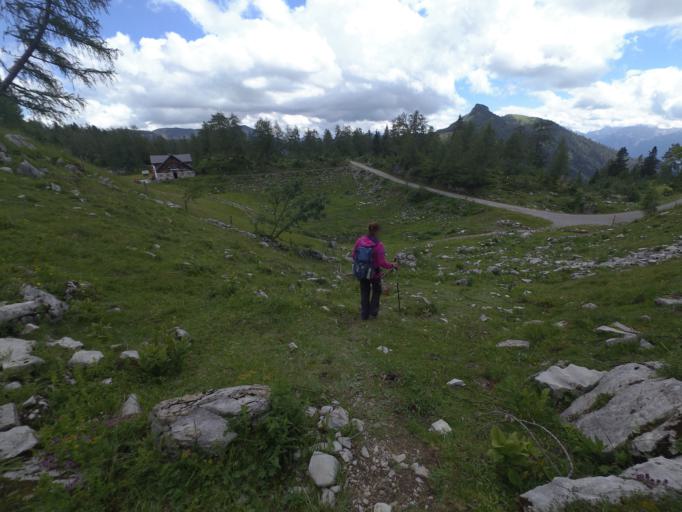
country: AT
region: Salzburg
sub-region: Politischer Bezirk Salzburg-Umgebung
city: Hintersee
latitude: 47.6615
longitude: 13.3018
